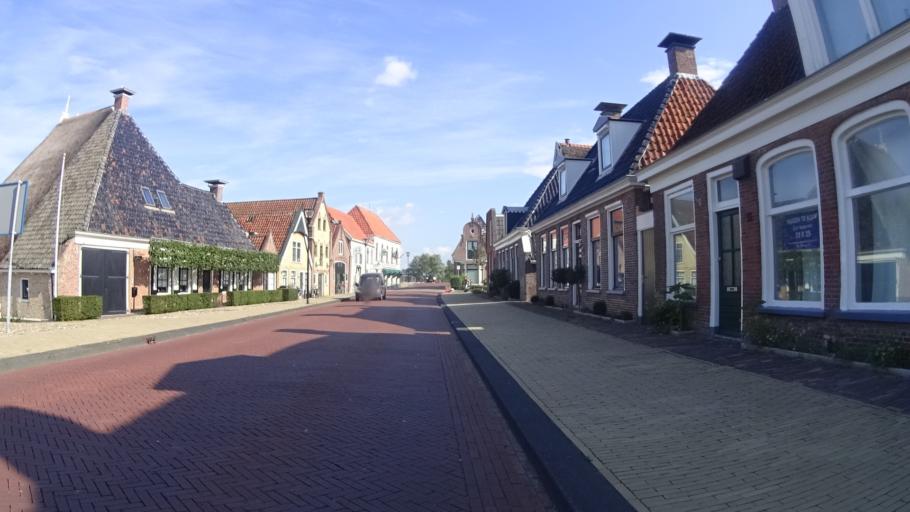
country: NL
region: Friesland
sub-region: Gemeente Franekeradeel
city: Franeker
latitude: 53.1857
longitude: 5.5488
